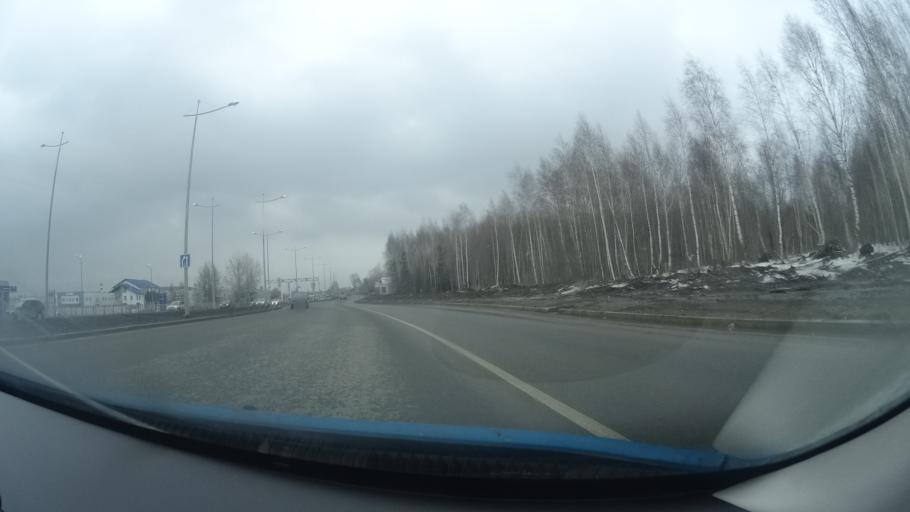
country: RU
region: Perm
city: Kondratovo
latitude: 57.9432
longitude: 56.0706
